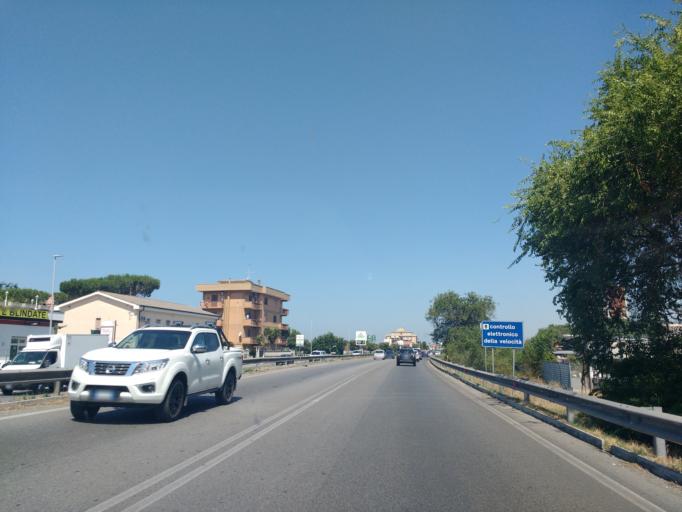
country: IT
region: Latium
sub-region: Citta metropolitana di Roma Capitale
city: Lido di Ostia
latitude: 41.7597
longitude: 12.2703
